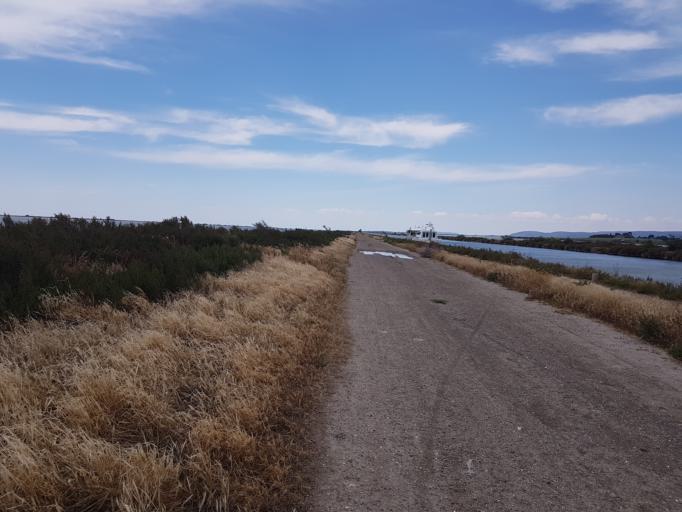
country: FR
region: Languedoc-Roussillon
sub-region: Departement de l'Herault
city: Villeneuve-les-Maguelone
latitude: 43.5137
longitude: 3.8765
